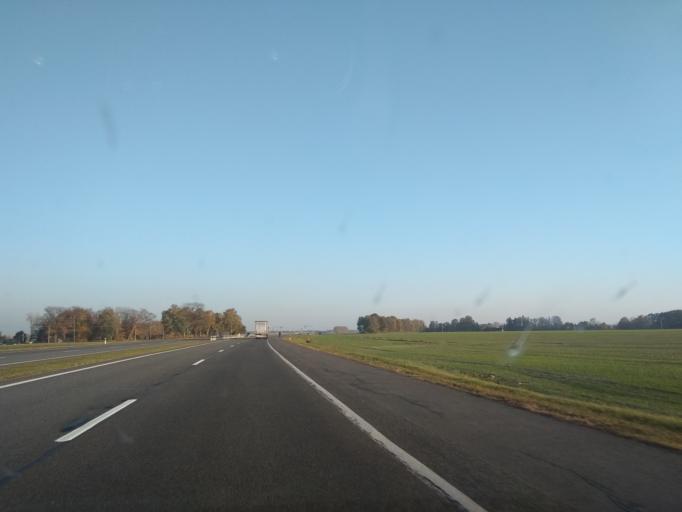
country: BY
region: Brest
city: Kobryn
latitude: 52.1973
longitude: 24.2989
